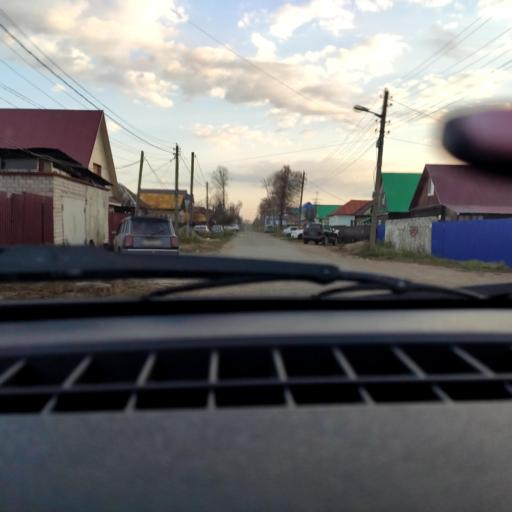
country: RU
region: Bashkortostan
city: Iglino
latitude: 54.8297
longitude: 56.1823
